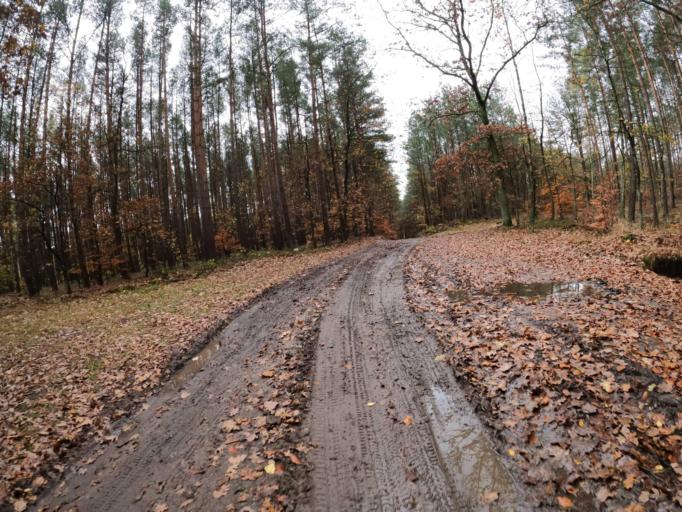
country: PL
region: West Pomeranian Voivodeship
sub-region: Powiat walecki
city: Tuczno
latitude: 53.2702
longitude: 16.2430
